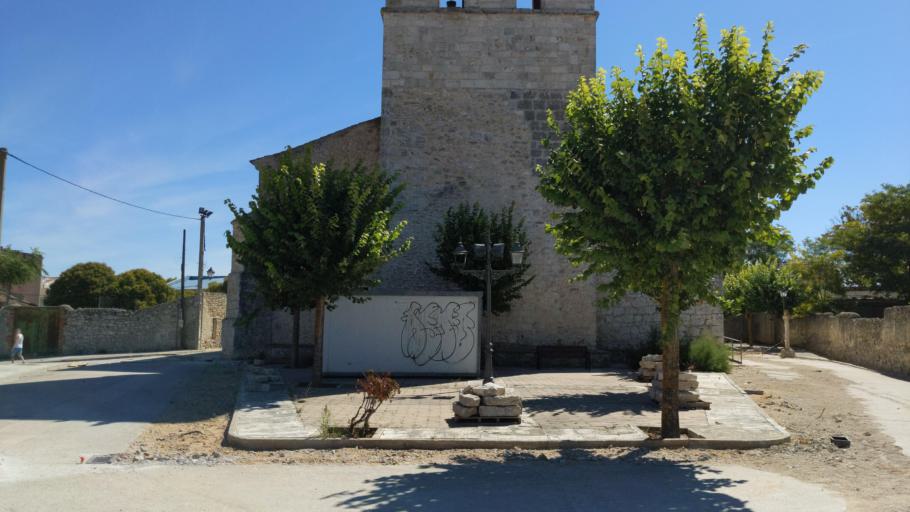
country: ES
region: Castille and Leon
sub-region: Provincia de Valladolid
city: Tudela de Duero
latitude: 41.5368
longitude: -4.5355
